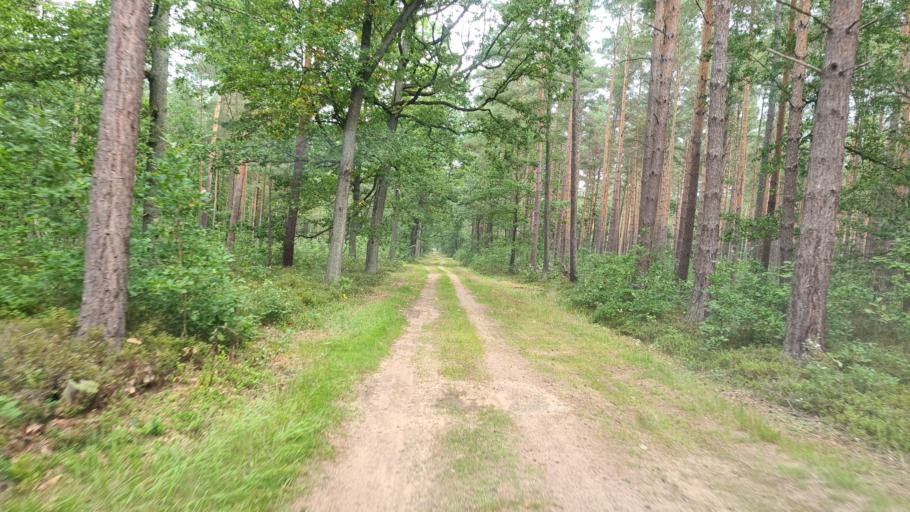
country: DE
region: Brandenburg
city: Hohenbucko
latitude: 51.7836
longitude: 13.5437
